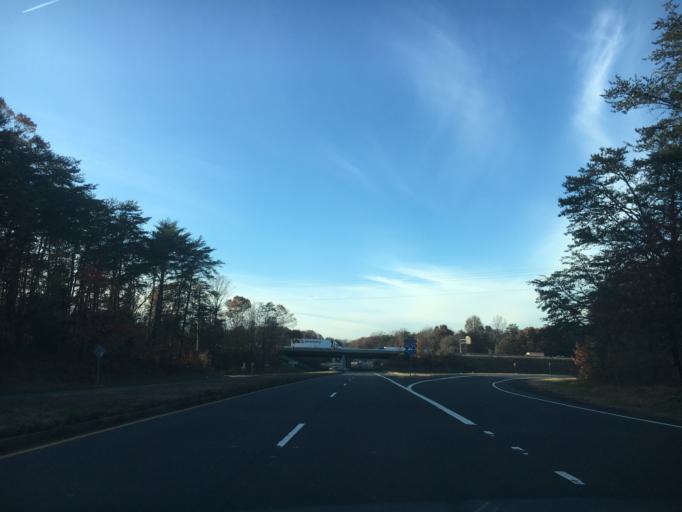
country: US
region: Virginia
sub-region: Prince William County
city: Triangle
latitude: 38.5485
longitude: -77.3412
